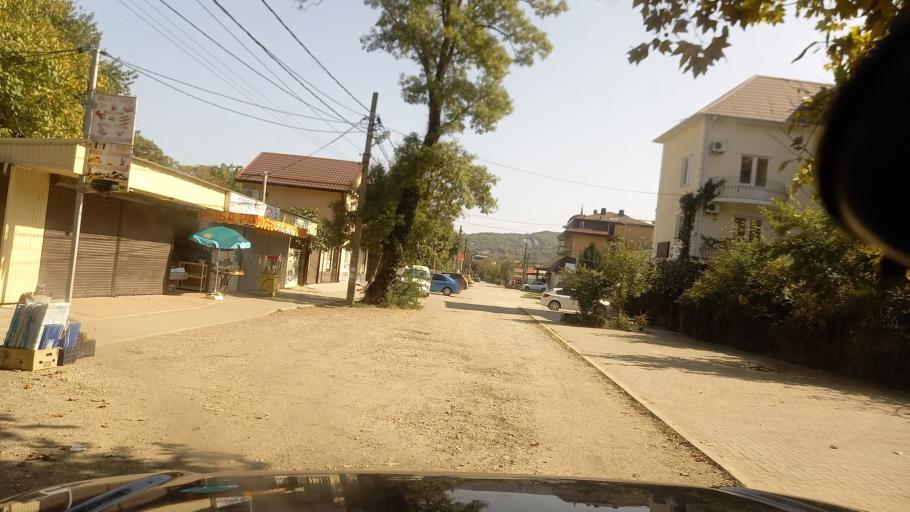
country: RU
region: Krasnodarskiy
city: Arkhipo-Osipovka
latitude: 44.3652
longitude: 38.5234
